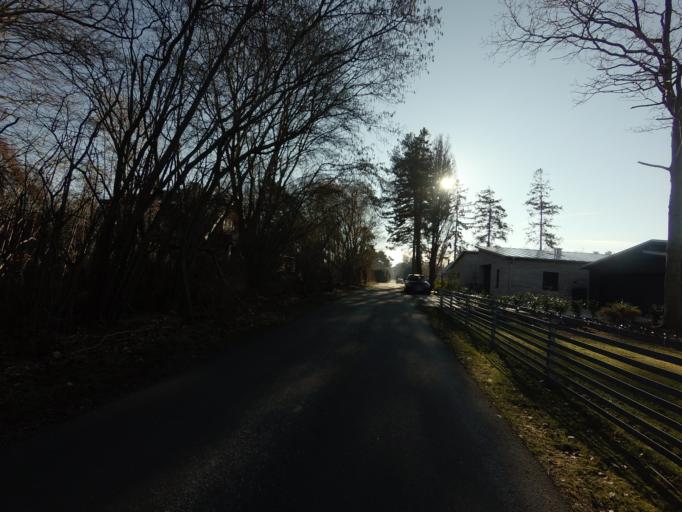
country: SE
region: Skane
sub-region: Vellinge Kommun
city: Hollviken
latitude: 55.4191
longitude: 12.9646
